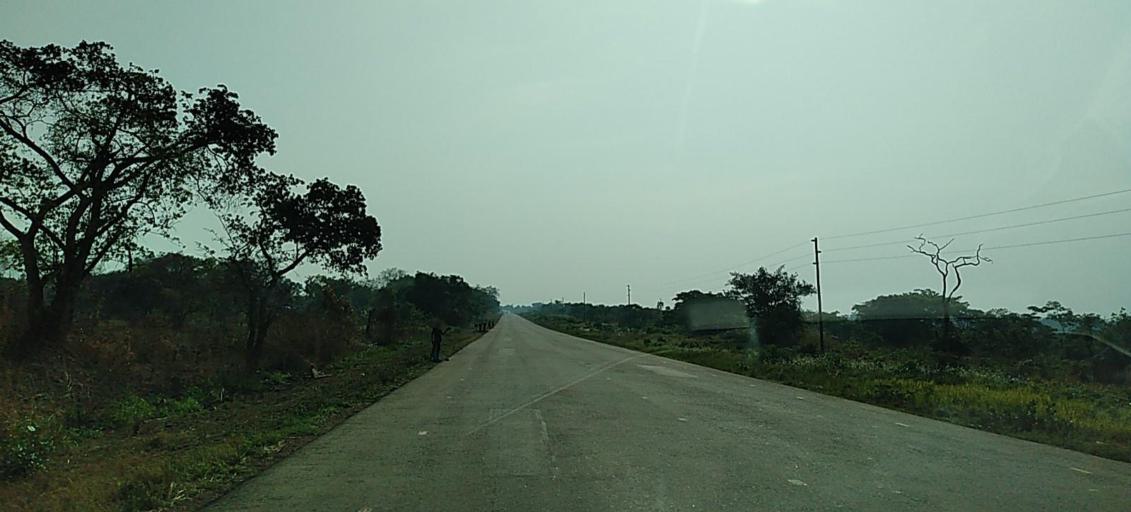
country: ZM
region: North-Western
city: Kansanshi
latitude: -12.3118
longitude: 26.9577
